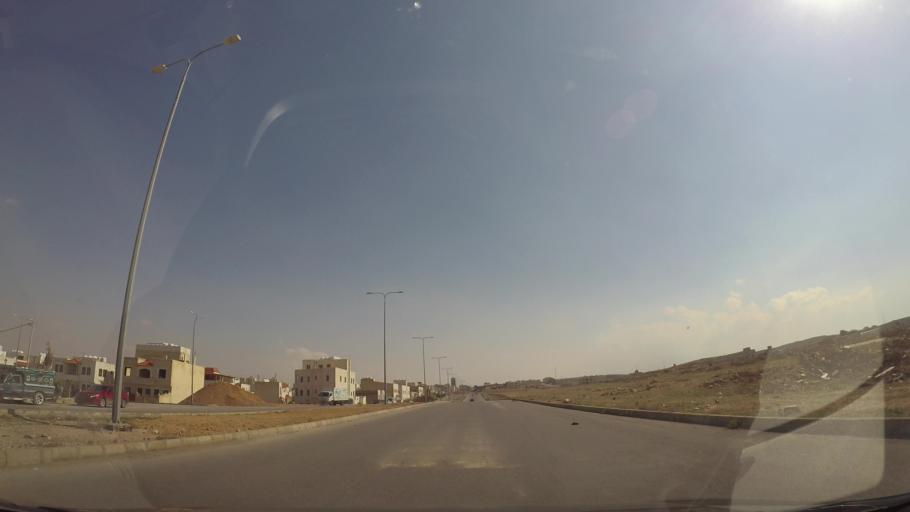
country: JO
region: Zarqa
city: Zarqa
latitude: 32.0585
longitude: 36.1137
